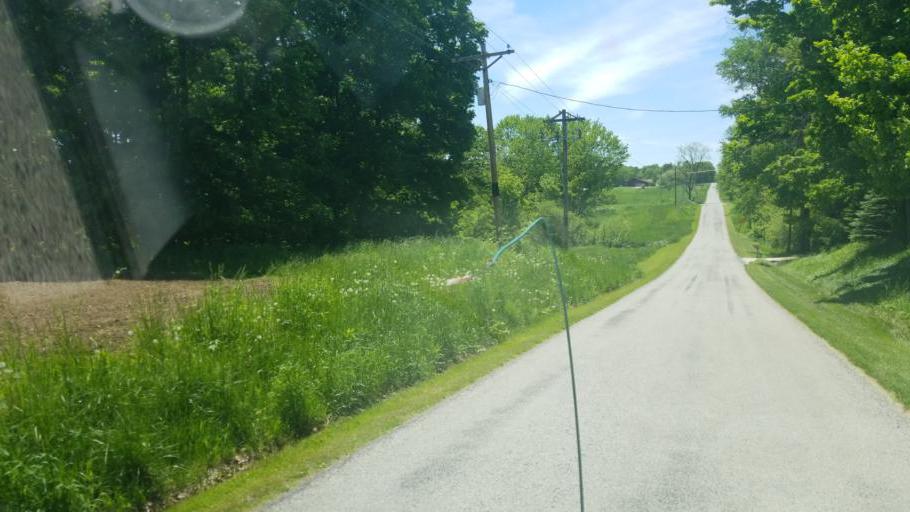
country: US
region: Ohio
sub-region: Huron County
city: Willard
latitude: 41.1200
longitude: -82.6830
